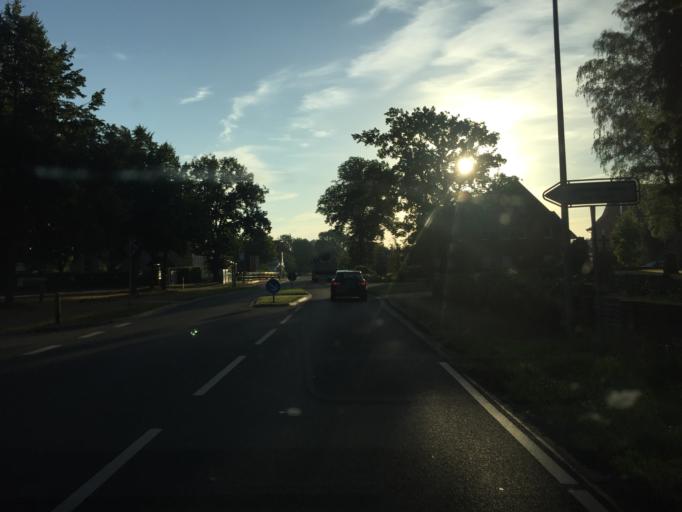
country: DE
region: Lower Saxony
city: Heemsen
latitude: 52.7043
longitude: 9.2625
